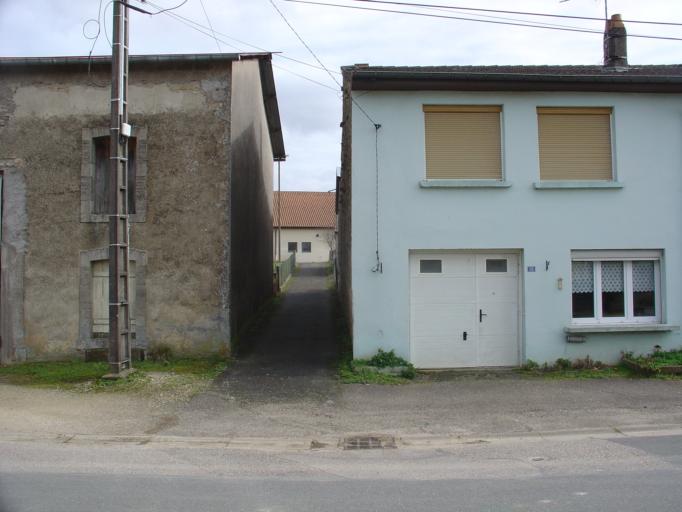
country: FR
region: Lorraine
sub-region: Departement de Meurthe-et-Moselle
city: Colombey-les-Belles
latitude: 48.5578
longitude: 5.8818
